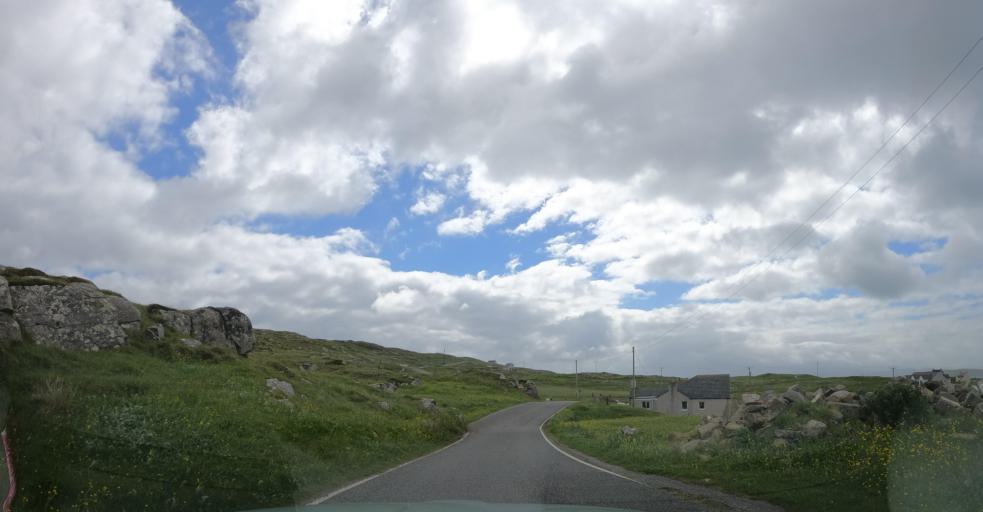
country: GB
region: Scotland
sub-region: Eilean Siar
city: Isle of South Uist
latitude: 57.0828
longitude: -7.3034
